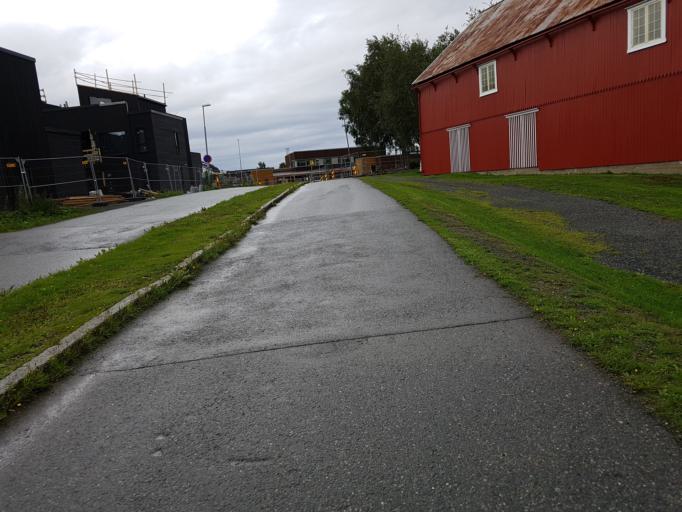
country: NO
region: Sor-Trondelag
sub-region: Trondheim
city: Trondheim
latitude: 63.3874
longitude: 10.4281
